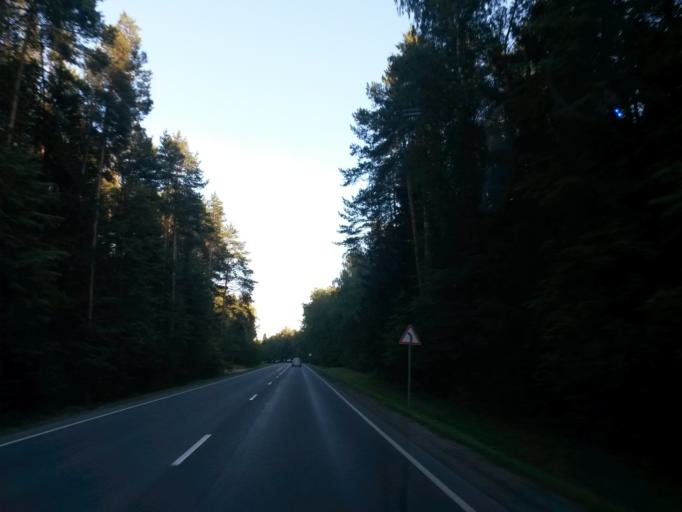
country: RU
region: Moskovskaya
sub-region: Podol'skiy Rayon
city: Podol'sk
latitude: 55.3794
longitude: 37.6351
